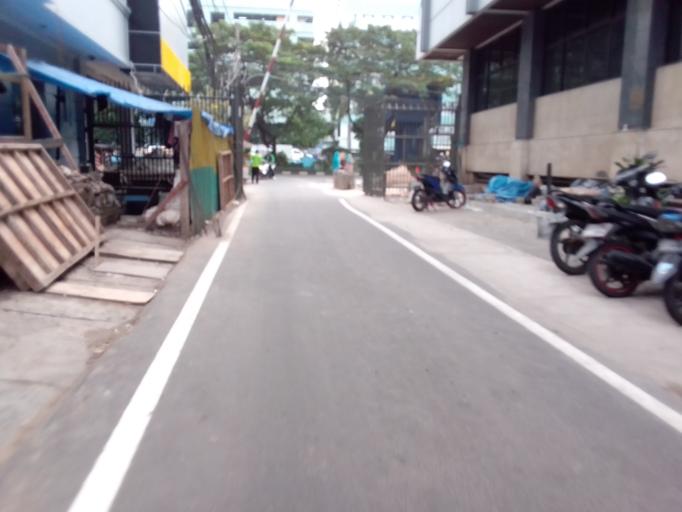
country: ID
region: Jakarta Raya
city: Jakarta
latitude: -6.1716
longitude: 106.8115
